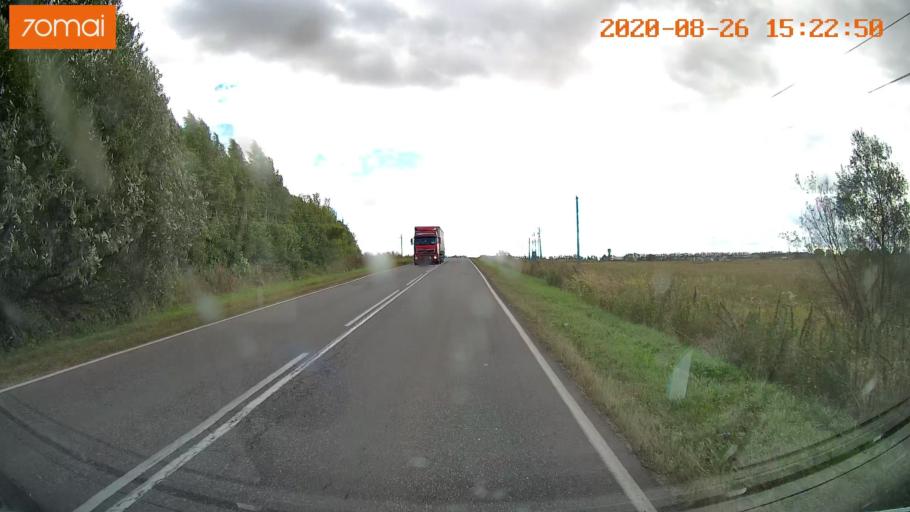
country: RU
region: Tula
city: Severo-Zadonsk
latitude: 54.1253
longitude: 38.4556
